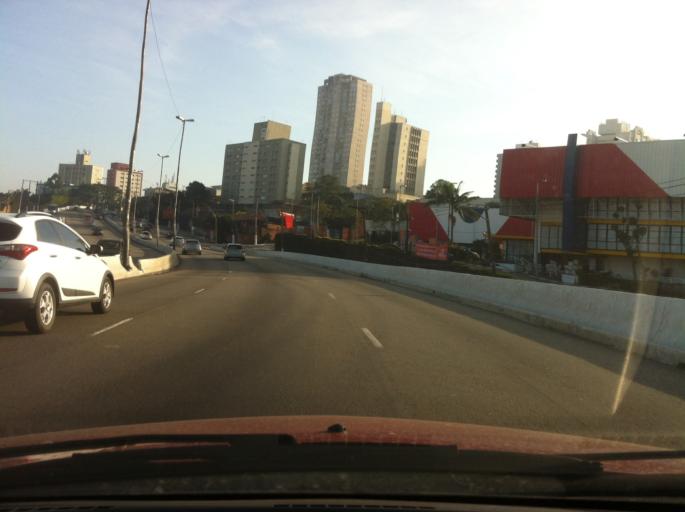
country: BR
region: Sao Paulo
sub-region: Diadema
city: Diadema
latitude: -23.6431
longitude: -46.6723
